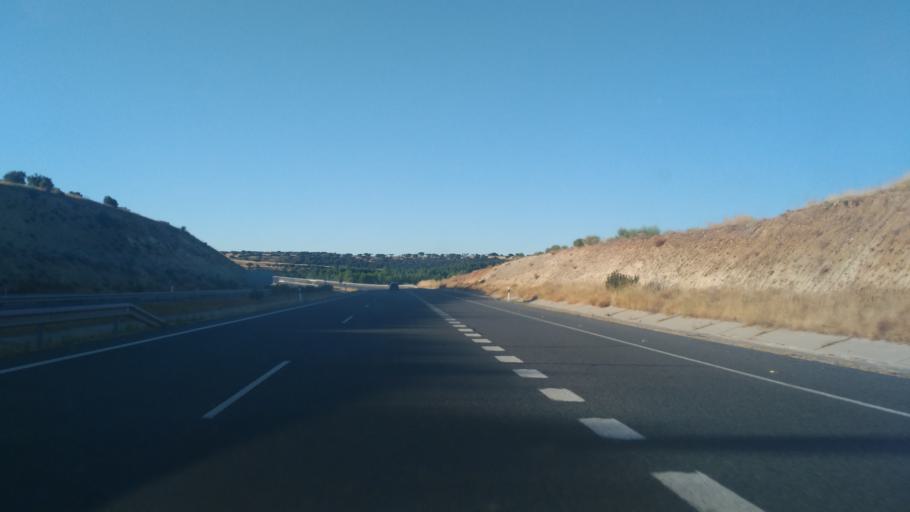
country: ES
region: Castille and Leon
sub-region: Provincia de Salamanca
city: Belena
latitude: 40.7079
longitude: -5.6237
